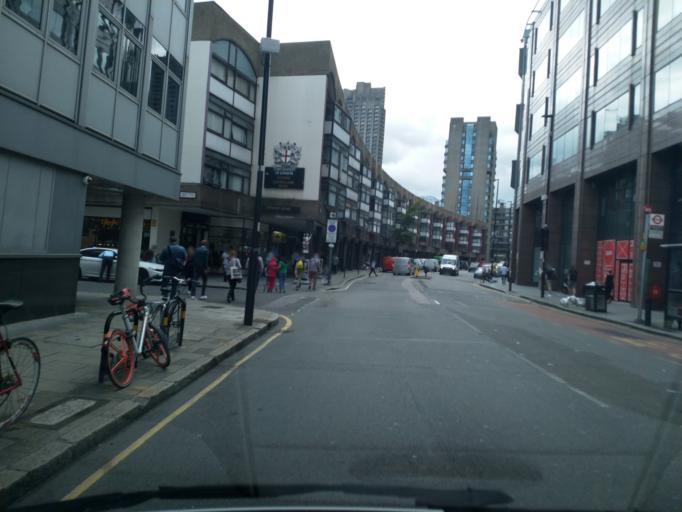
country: GB
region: England
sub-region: Greater London
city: Barbican
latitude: 51.5231
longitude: -0.0981
